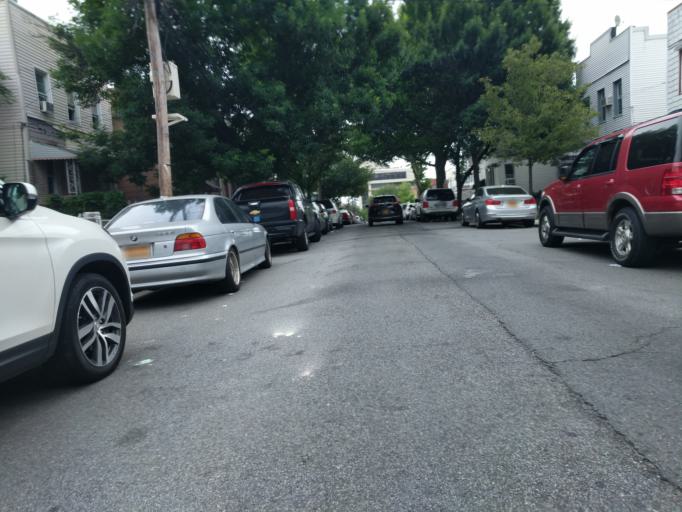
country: US
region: New York
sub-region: Queens County
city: Borough of Queens
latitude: 40.7435
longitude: -73.8543
